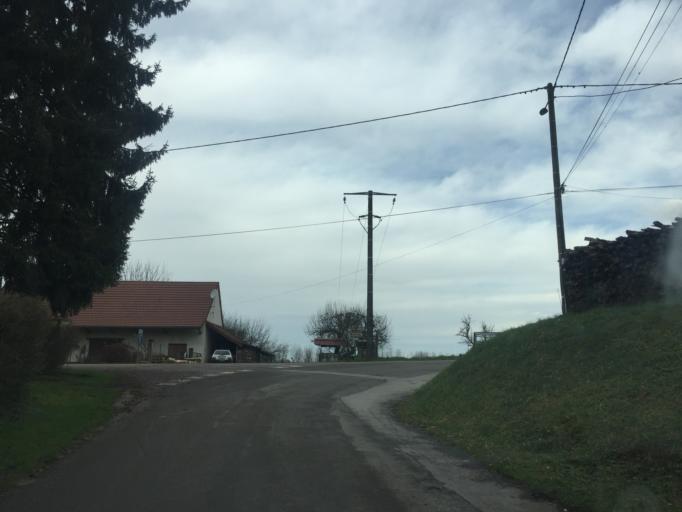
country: FR
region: Franche-Comte
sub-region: Departement du Jura
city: Chaussin
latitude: 46.9016
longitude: 5.4535
